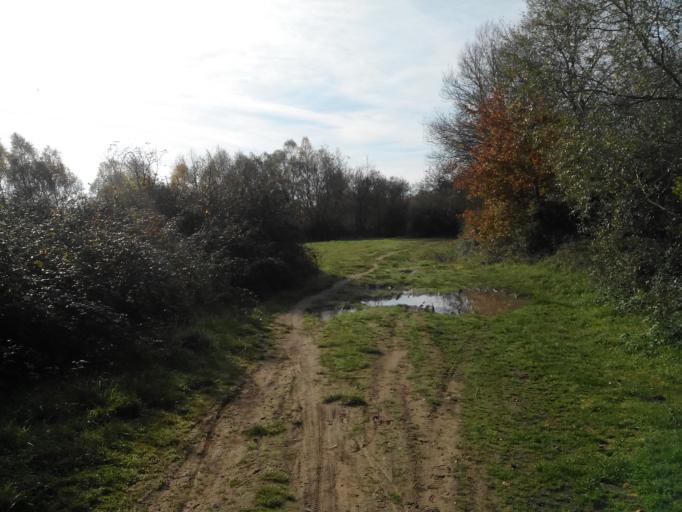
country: FR
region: Centre
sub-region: Departement d'Indre-et-Loire
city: Fondettes
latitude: 47.3821
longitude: 0.6091
